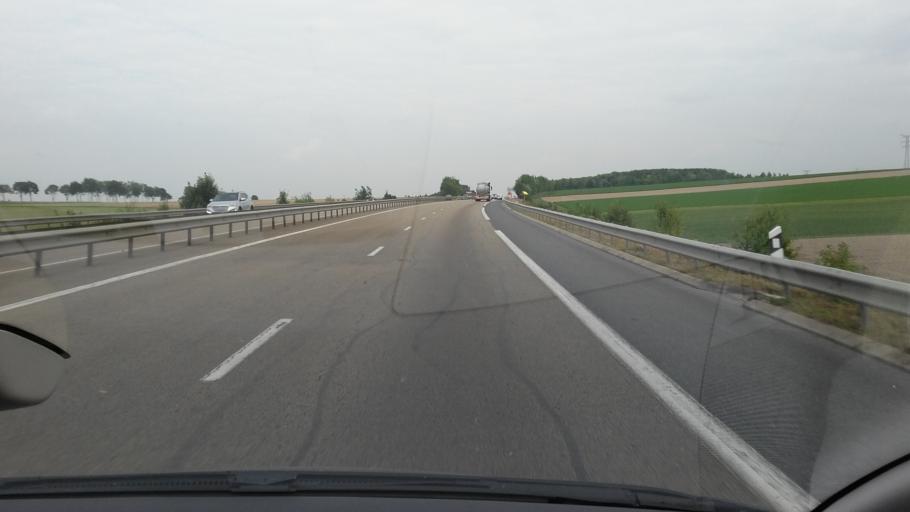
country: FR
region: Champagne-Ardenne
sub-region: Departement de la Marne
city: Cernay-les-Reims
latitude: 49.2768
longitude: 4.0971
